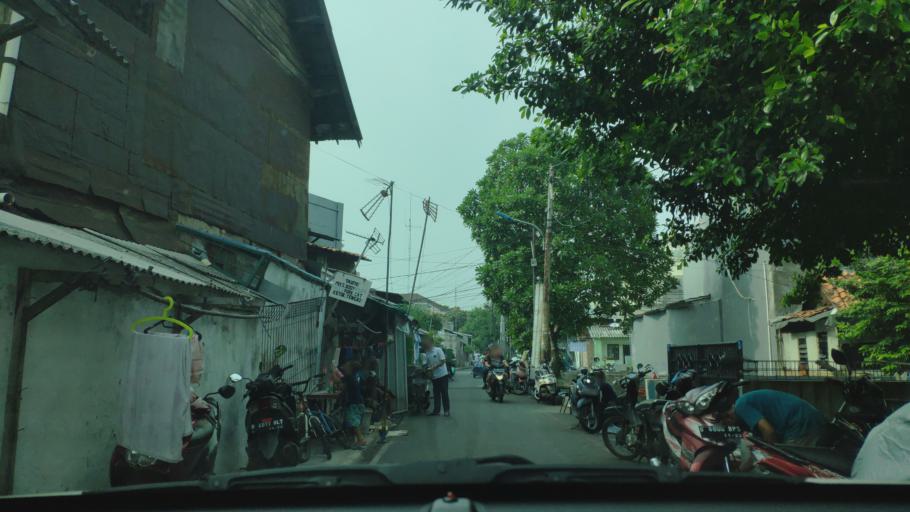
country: ID
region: Jakarta Raya
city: Jakarta
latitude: -6.1572
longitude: 106.8228
